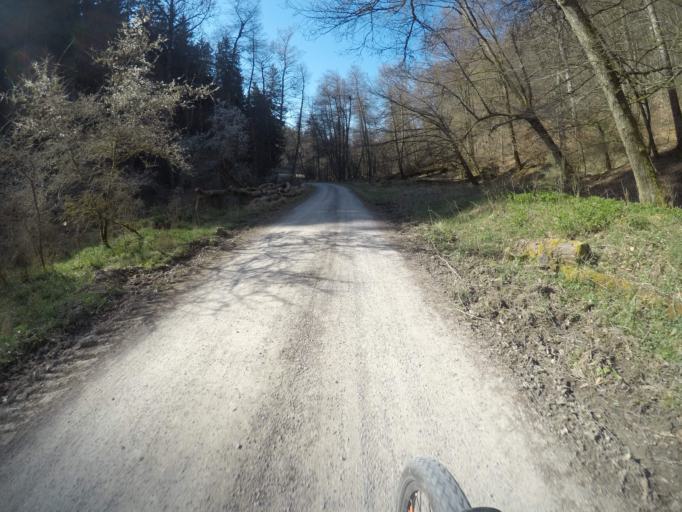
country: DE
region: Baden-Wuerttemberg
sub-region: Regierungsbezirk Stuttgart
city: Weil im Schonbuch
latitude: 48.5820
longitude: 9.0380
